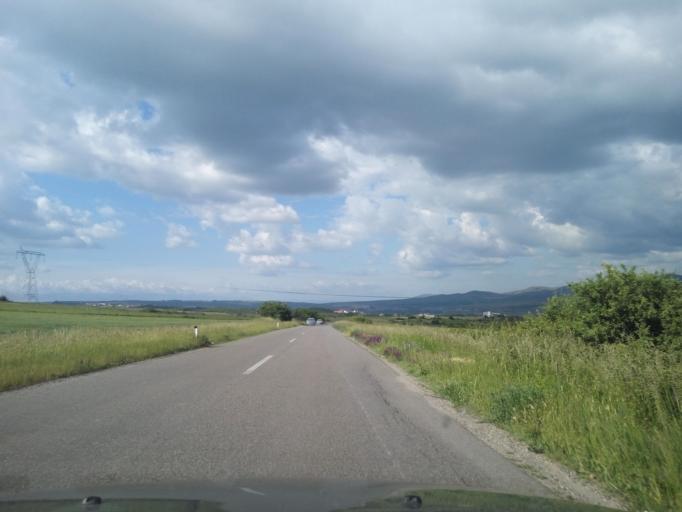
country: XK
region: Gjakova
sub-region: Komuna e Gjakoves
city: Gjakove
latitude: 42.4452
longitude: 20.4922
